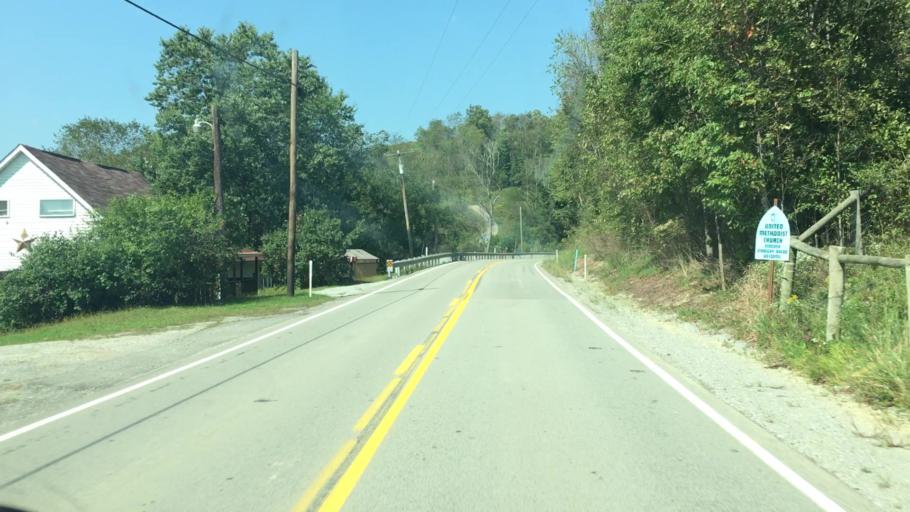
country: US
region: Pennsylvania
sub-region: Greene County
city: Waynesburg
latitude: 39.9541
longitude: -80.3050
